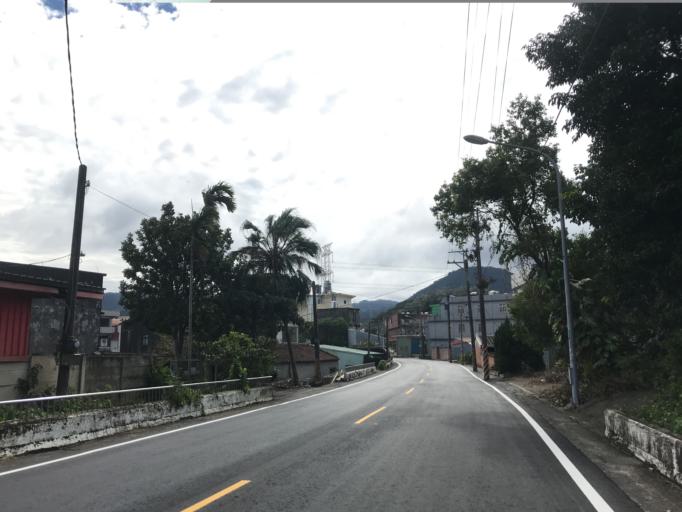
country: TW
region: Taiwan
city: Daxi
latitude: 24.8333
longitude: 121.2442
